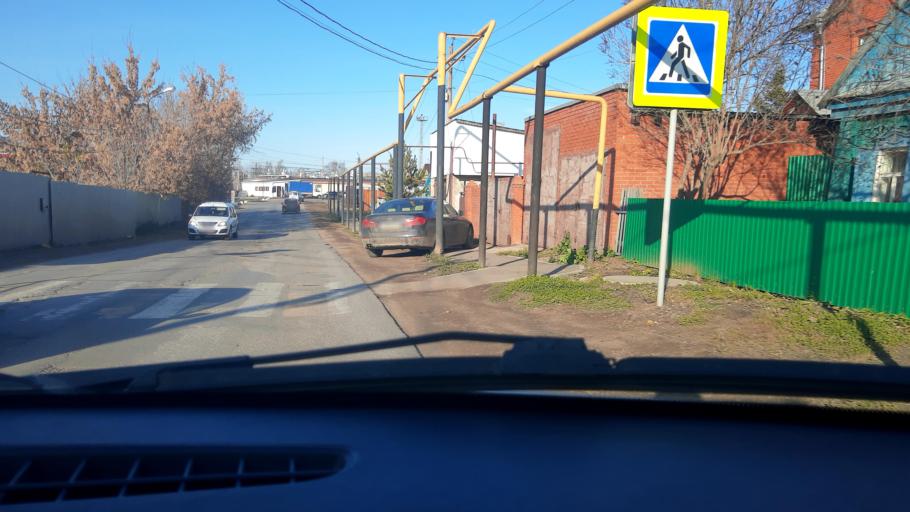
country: RU
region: Bashkortostan
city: Mikhaylovka
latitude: 54.6988
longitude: 55.8493
